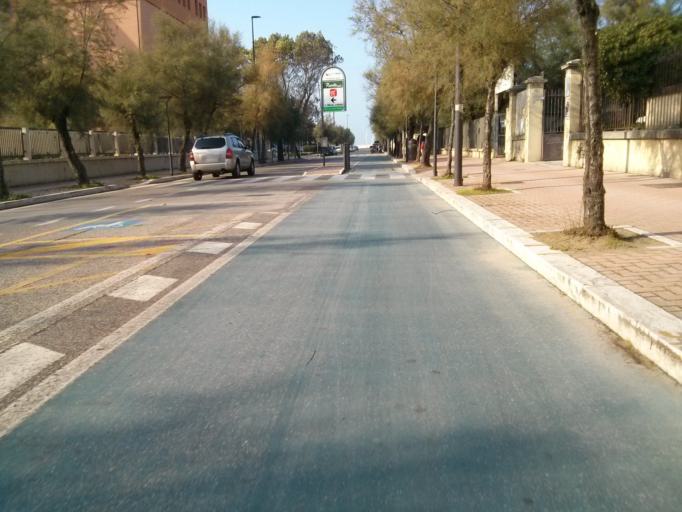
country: IT
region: The Marches
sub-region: Provincia di Pesaro e Urbino
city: Pesaro
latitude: 43.9205
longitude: 12.9085
